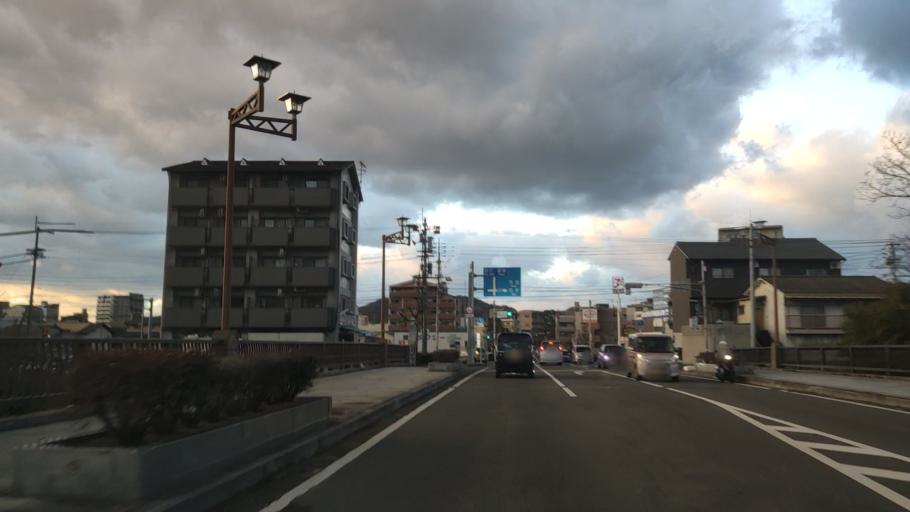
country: JP
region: Ehime
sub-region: Shikoku-chuo Shi
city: Matsuyama
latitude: 33.8397
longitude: 132.7857
